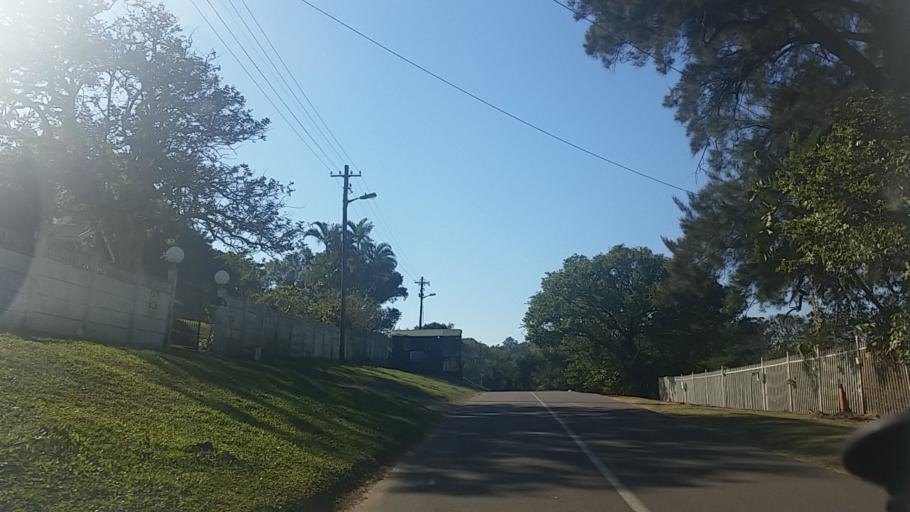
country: ZA
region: KwaZulu-Natal
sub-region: eThekwini Metropolitan Municipality
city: Berea
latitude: -29.8453
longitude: 30.9046
